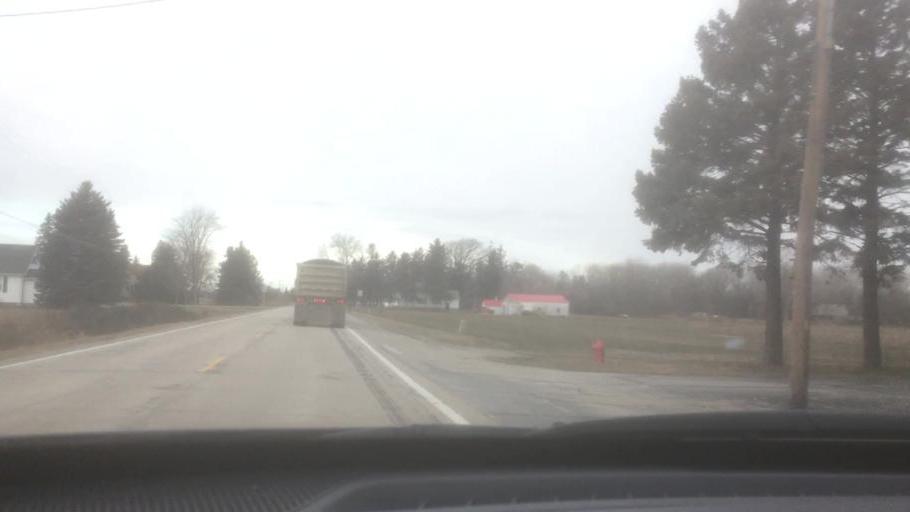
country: US
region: Michigan
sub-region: Bay County
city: Essexville
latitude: 43.5221
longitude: -83.7838
